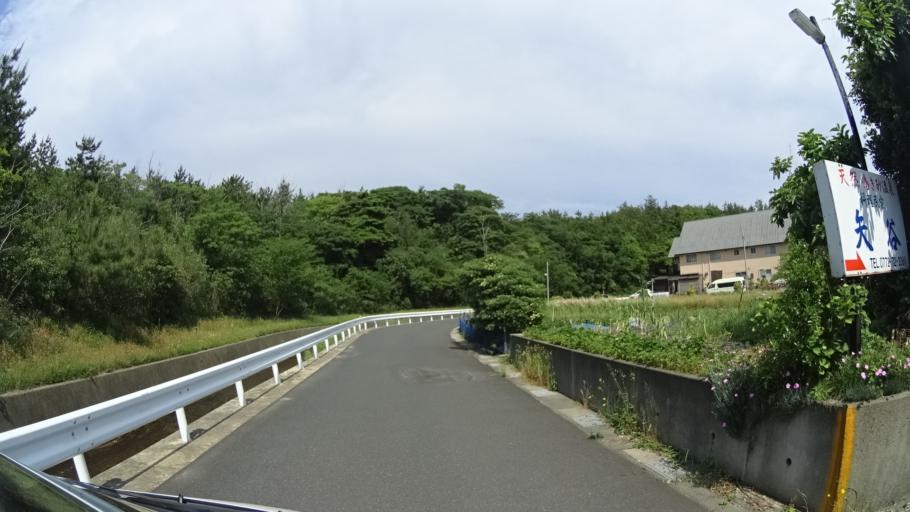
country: JP
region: Kyoto
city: Miyazu
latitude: 35.7016
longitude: 135.0534
